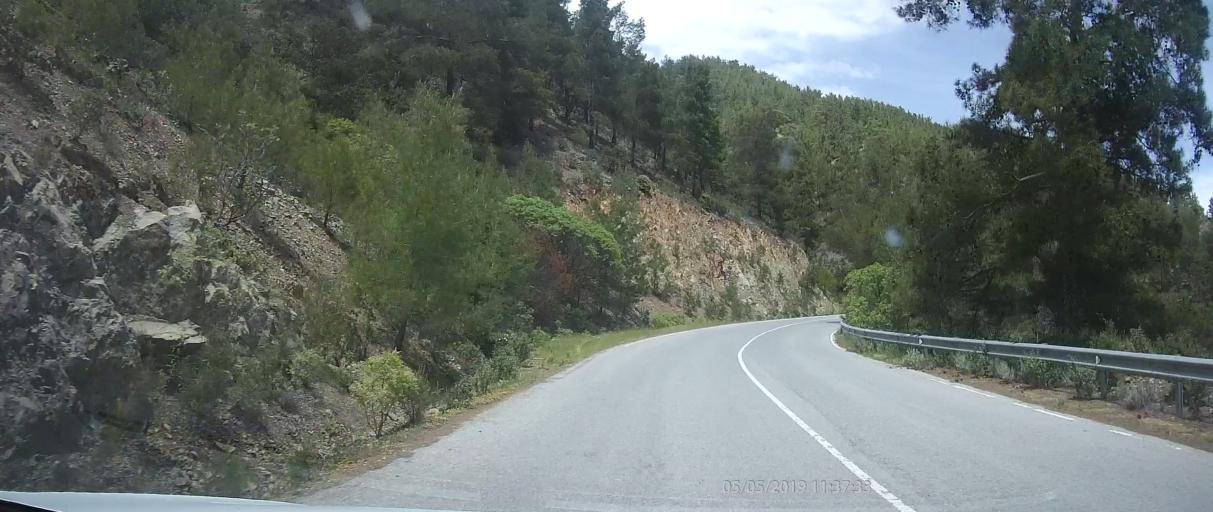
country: CY
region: Lefkosia
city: Kato Pyrgos
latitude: 34.9739
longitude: 32.6587
